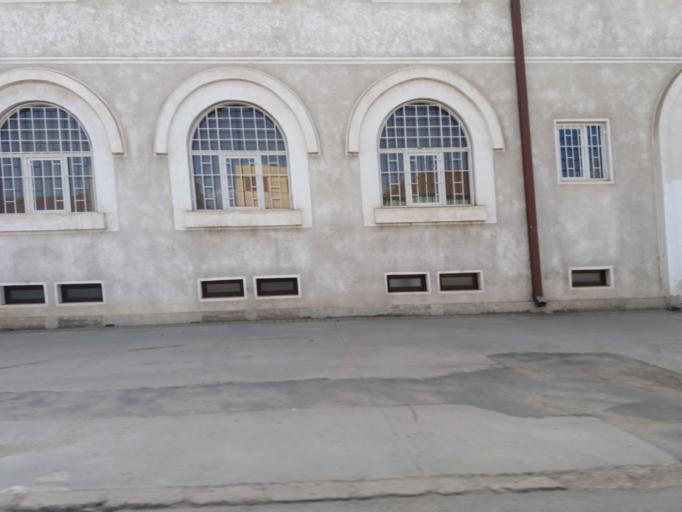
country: RO
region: Arad
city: Arad
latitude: 46.1892
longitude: 21.3289
